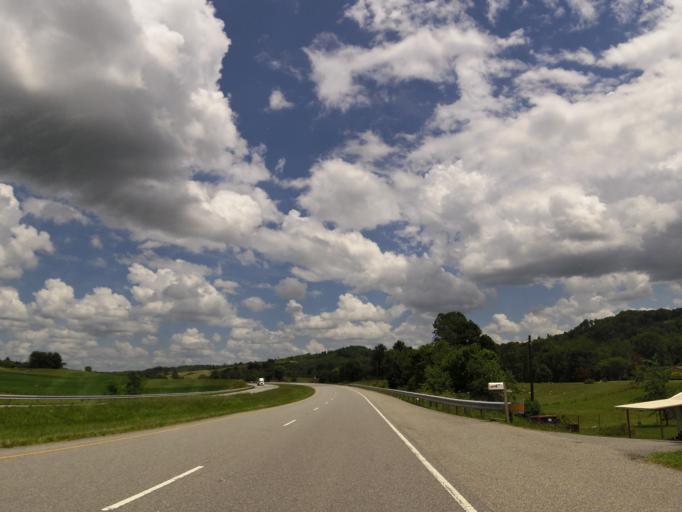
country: US
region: Tennessee
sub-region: Claiborne County
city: Harrogate
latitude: 36.6295
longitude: -83.4723
